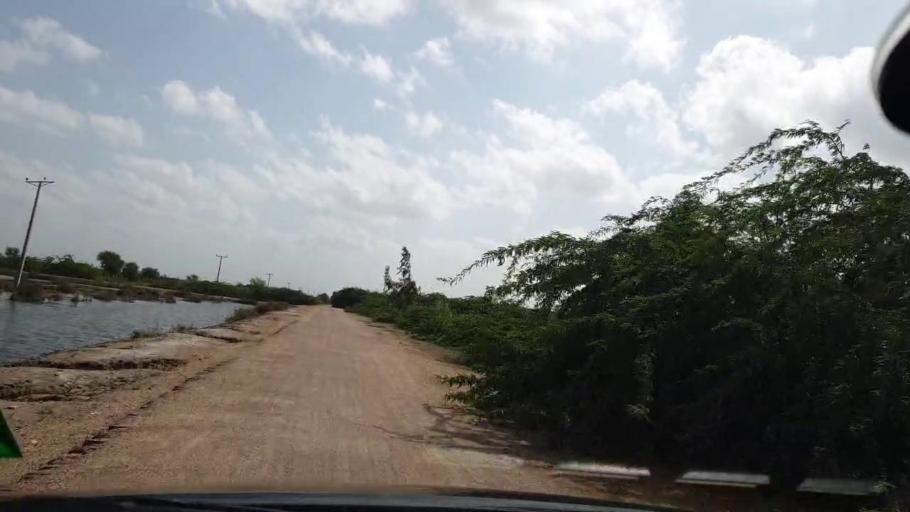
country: PK
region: Sindh
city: Kadhan
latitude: 24.5828
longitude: 69.1161
